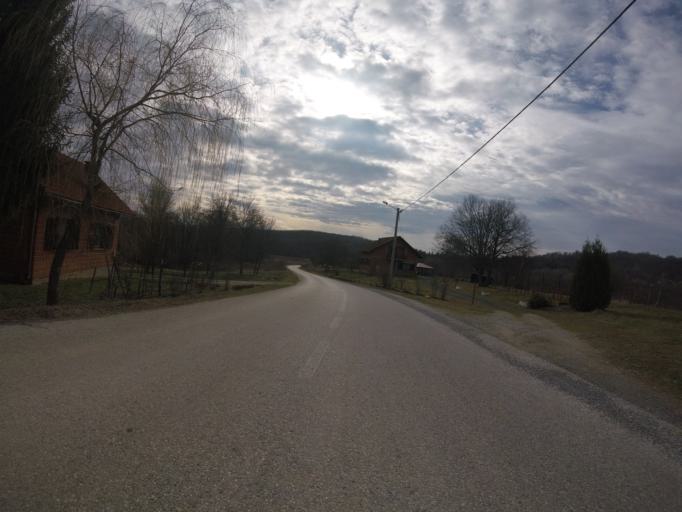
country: HR
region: Sisacko-Moslavacka
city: Glina
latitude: 45.4735
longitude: 16.0261
